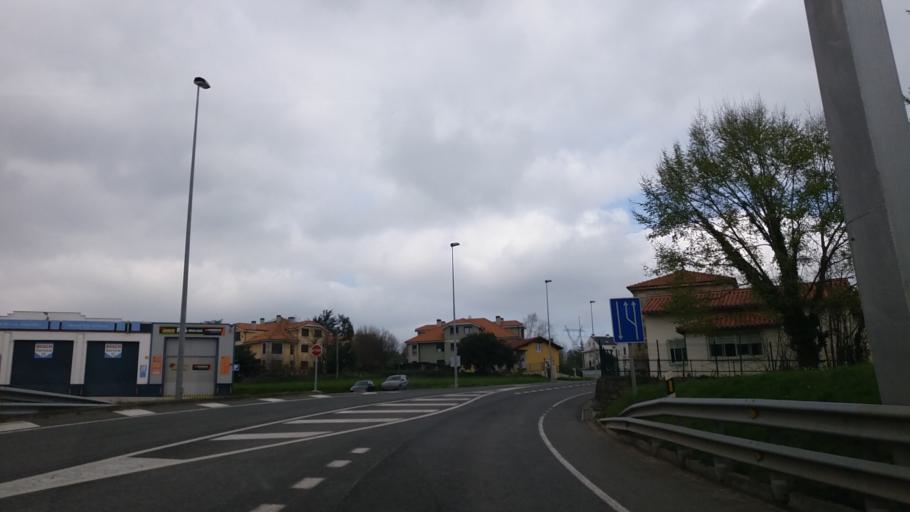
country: ES
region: Cantabria
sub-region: Provincia de Cantabria
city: Reocin
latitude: 43.3513
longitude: -4.1264
